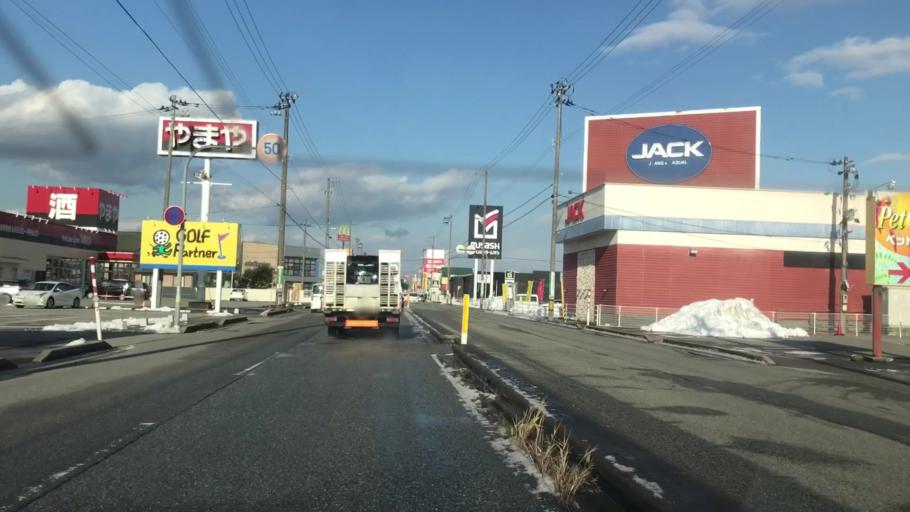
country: JP
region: Toyama
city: Toyama-shi
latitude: 36.6732
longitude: 137.2454
